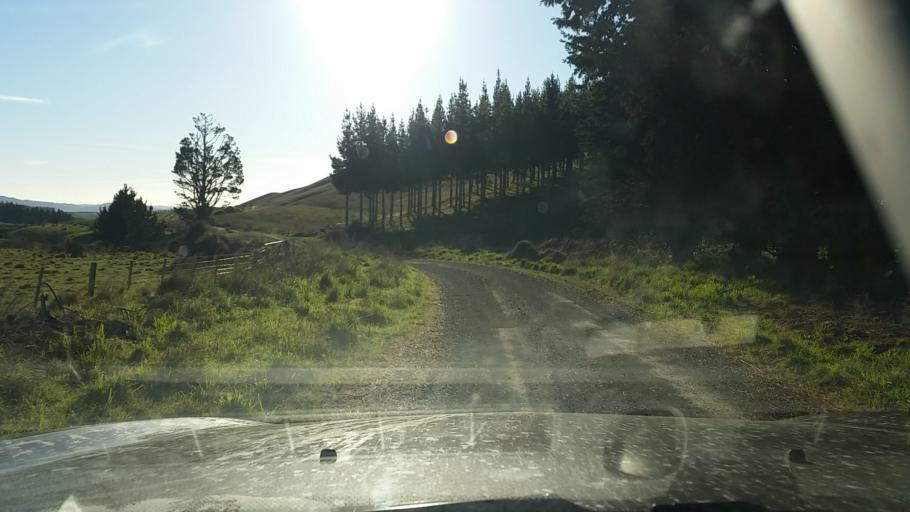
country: NZ
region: Marlborough
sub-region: Marlborough District
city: Blenheim
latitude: -41.7337
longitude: 174.0015
